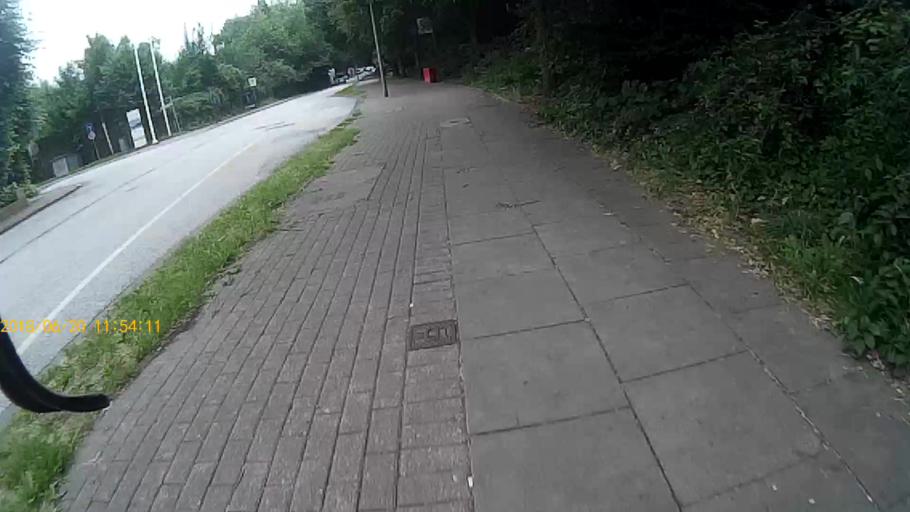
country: DE
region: Hamburg
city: Rothenburgsort
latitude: 53.5163
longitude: 10.0203
